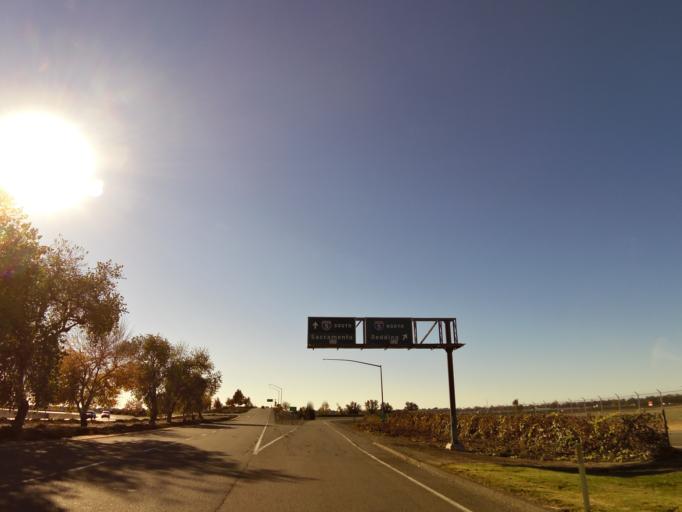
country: US
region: California
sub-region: Yolo County
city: West Sacramento
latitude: 38.6746
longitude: -121.5913
